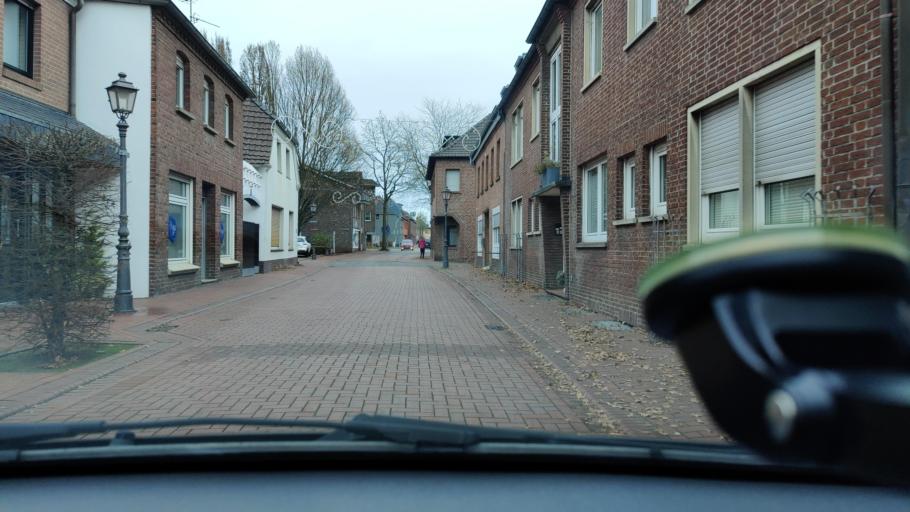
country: DE
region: North Rhine-Westphalia
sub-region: Regierungsbezirk Dusseldorf
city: Uedem
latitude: 51.6692
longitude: 6.2742
